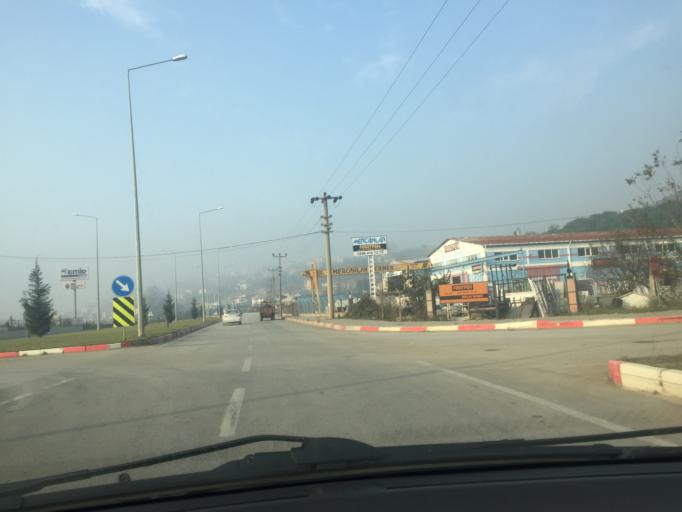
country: TR
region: Canakkale
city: Can
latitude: 40.0369
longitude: 27.0705
